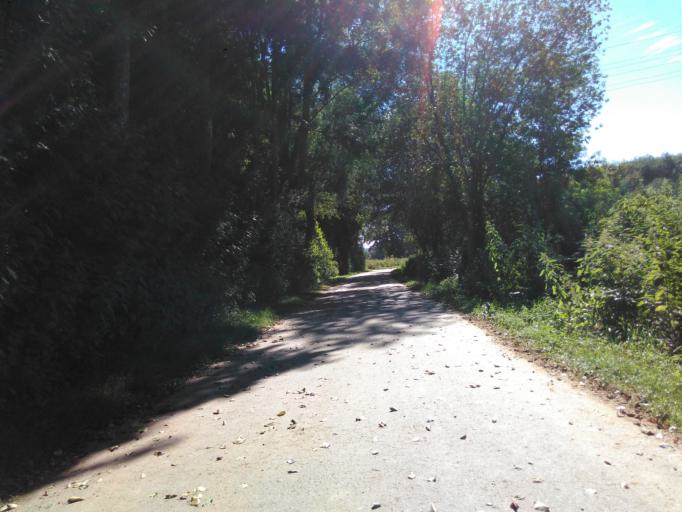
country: LU
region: Luxembourg
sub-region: Canton d'Esch-sur-Alzette
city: Sanem
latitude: 49.5511
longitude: 5.9405
